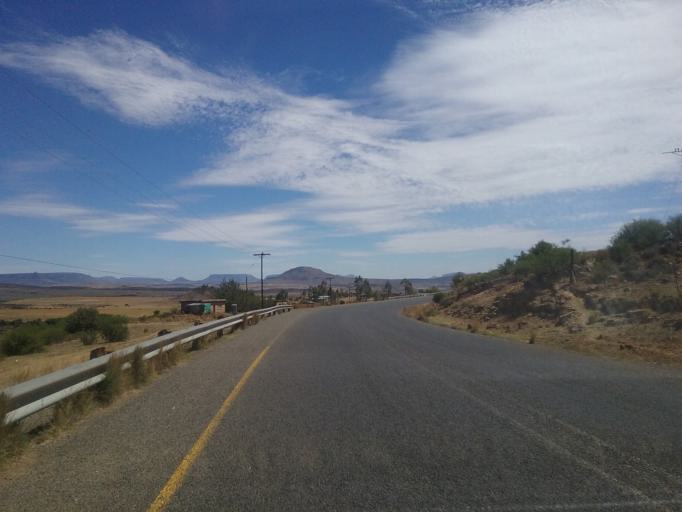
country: LS
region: Mohale's Hoek District
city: Mohale's Hoek
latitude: -30.1950
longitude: 27.4150
